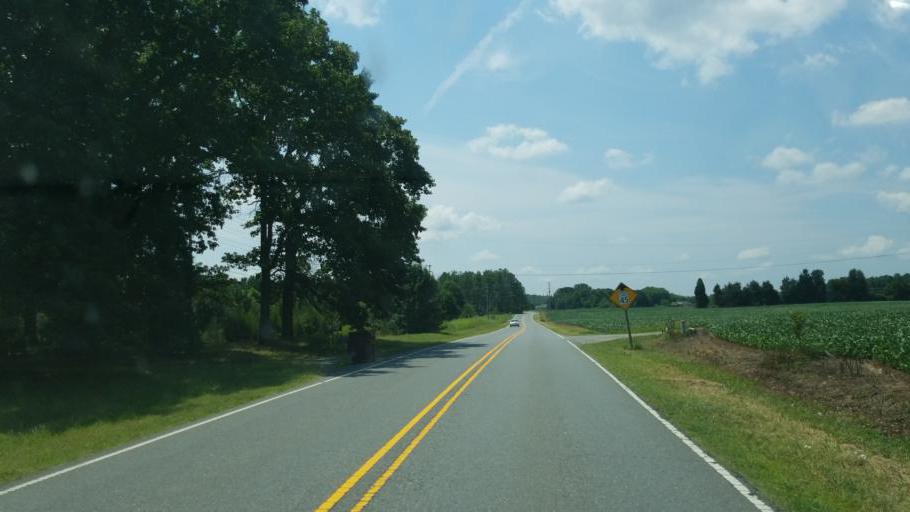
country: US
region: North Carolina
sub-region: Cleveland County
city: Kings Mountain
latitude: 35.2863
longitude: -81.3563
